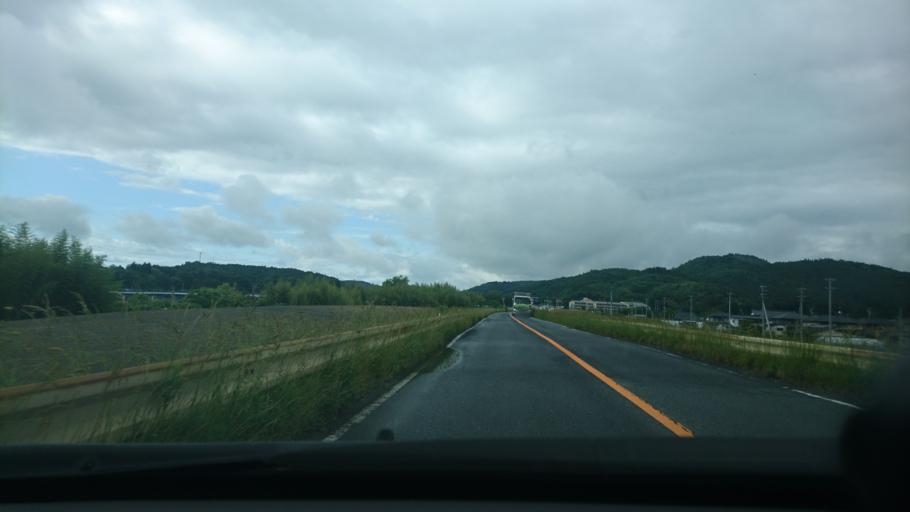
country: JP
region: Miyagi
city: Wakuya
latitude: 38.6497
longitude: 141.2868
